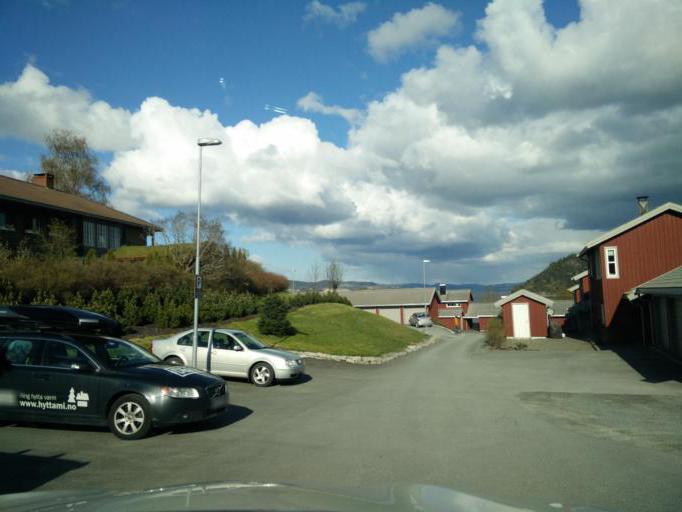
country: NO
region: Sor-Trondelag
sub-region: Skaun
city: Borsa
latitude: 63.3279
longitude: 10.0663
